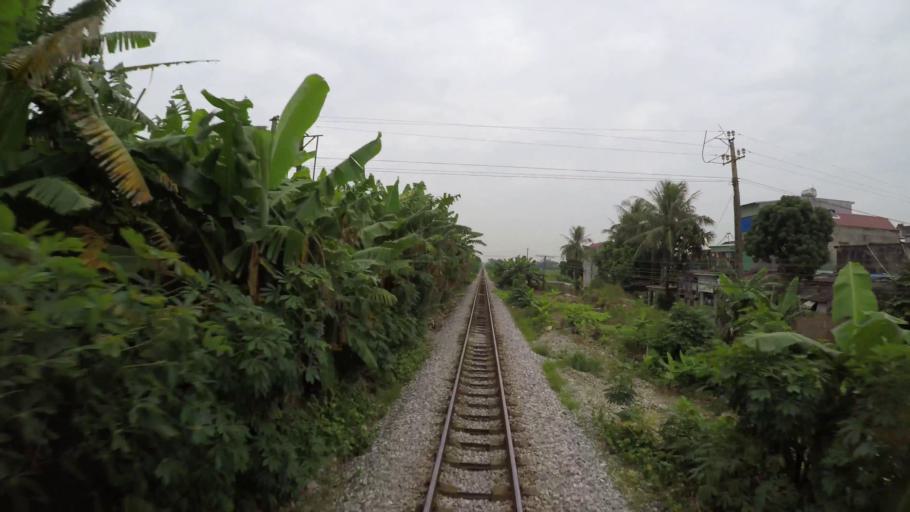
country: VN
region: Hai Phong
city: An Duong
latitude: 20.8940
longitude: 106.5885
